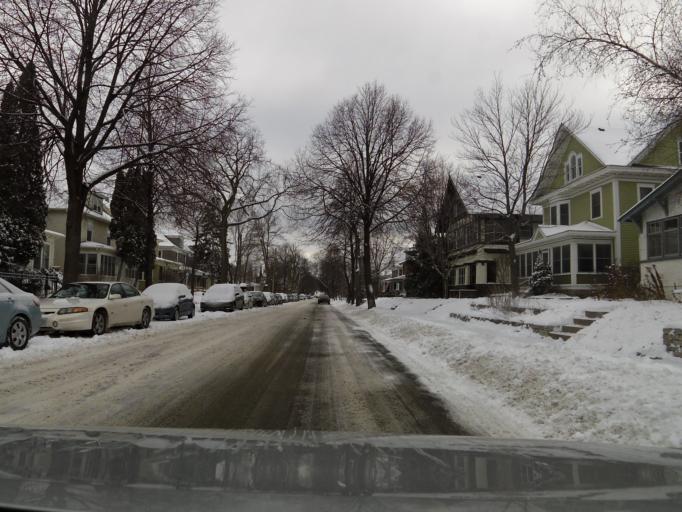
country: US
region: Minnesota
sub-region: Hennepin County
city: Saint Louis Park
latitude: 44.9458
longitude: -93.3009
